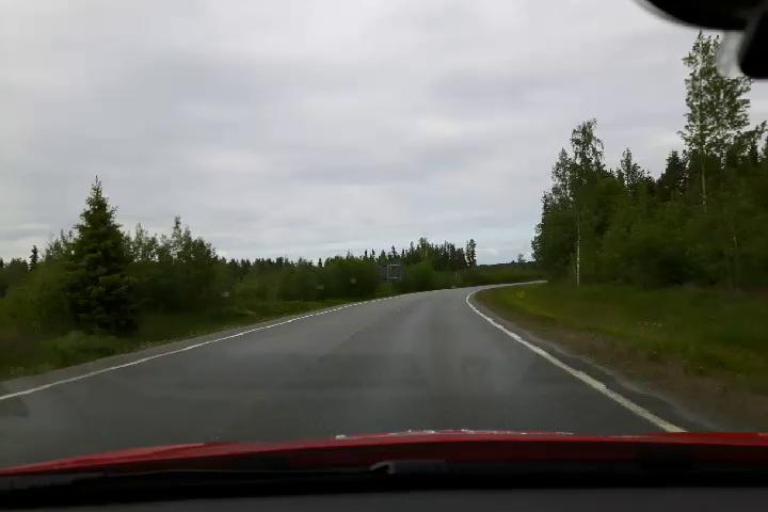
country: SE
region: Jaemtland
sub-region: Bergs Kommun
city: Hoverberg
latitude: 62.9163
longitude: 14.3281
